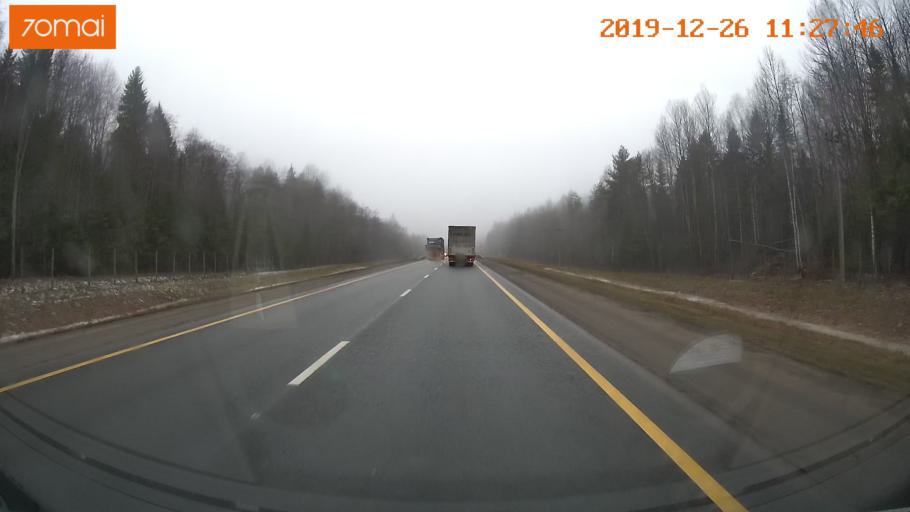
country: RU
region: Vologda
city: Chebsara
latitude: 59.1527
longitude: 38.8290
